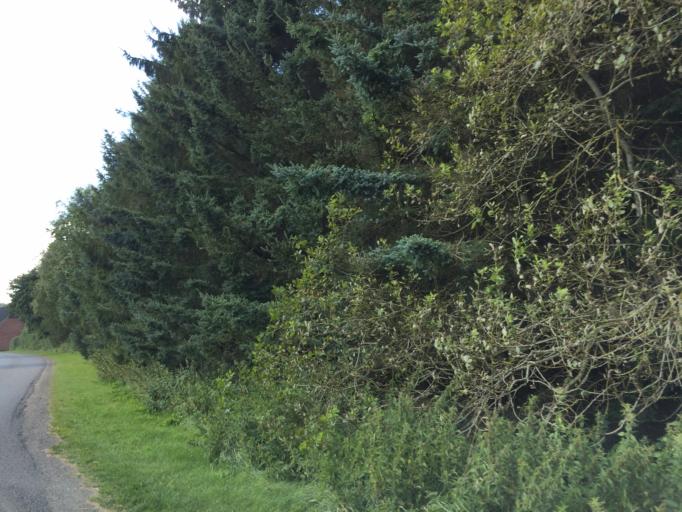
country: DK
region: Central Jutland
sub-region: Viborg Kommune
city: Viborg
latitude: 56.4896
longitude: 9.5255
